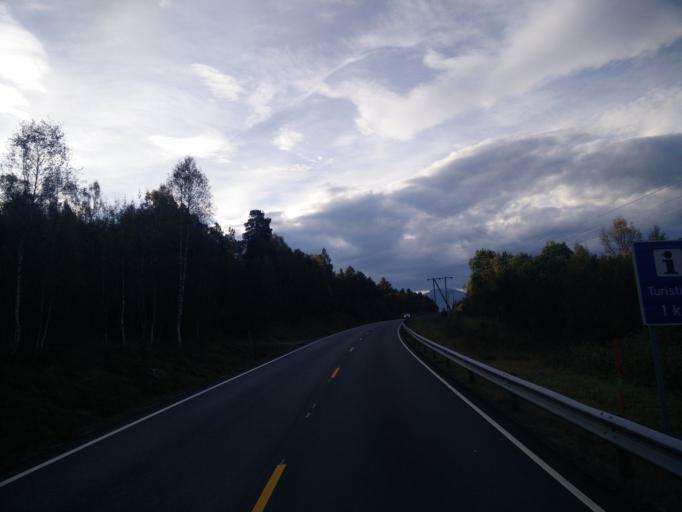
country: NO
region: More og Romsdal
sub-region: Gjemnes
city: Batnfjordsora
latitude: 62.8412
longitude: 7.5997
